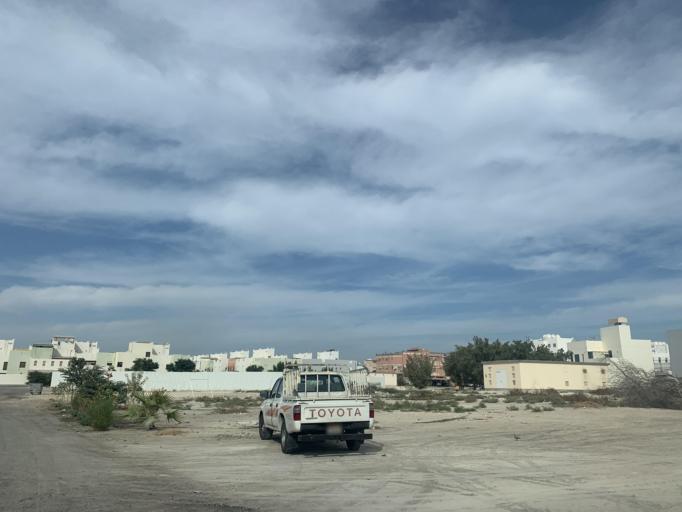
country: BH
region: Central Governorate
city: Madinat Hamad
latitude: 26.1204
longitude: 50.4758
